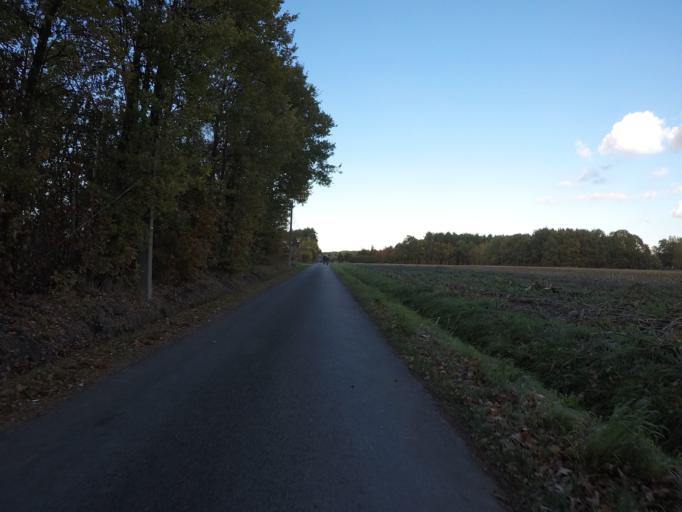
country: BE
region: Flanders
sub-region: Provincie Vlaams-Brabant
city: Begijnendijk
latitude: 51.0024
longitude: 4.8089
